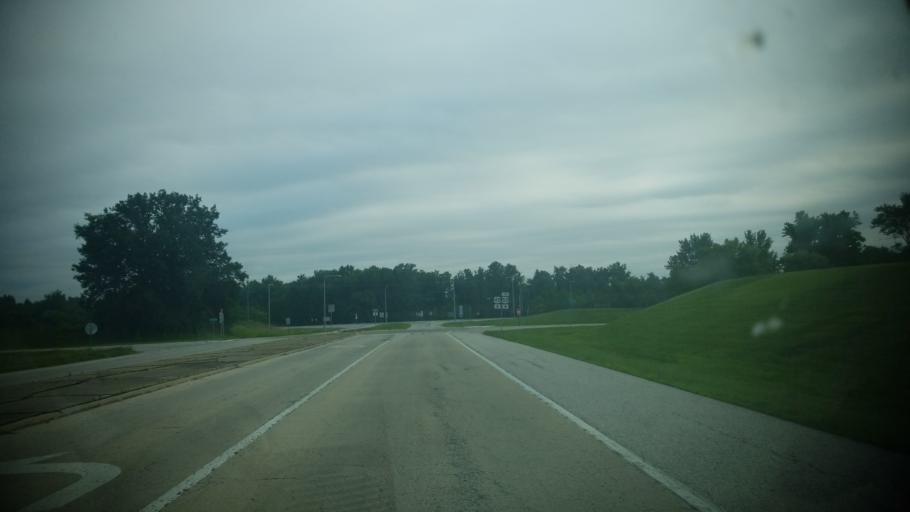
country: US
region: Illinois
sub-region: Clay County
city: Flora
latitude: 38.6725
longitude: -88.4381
